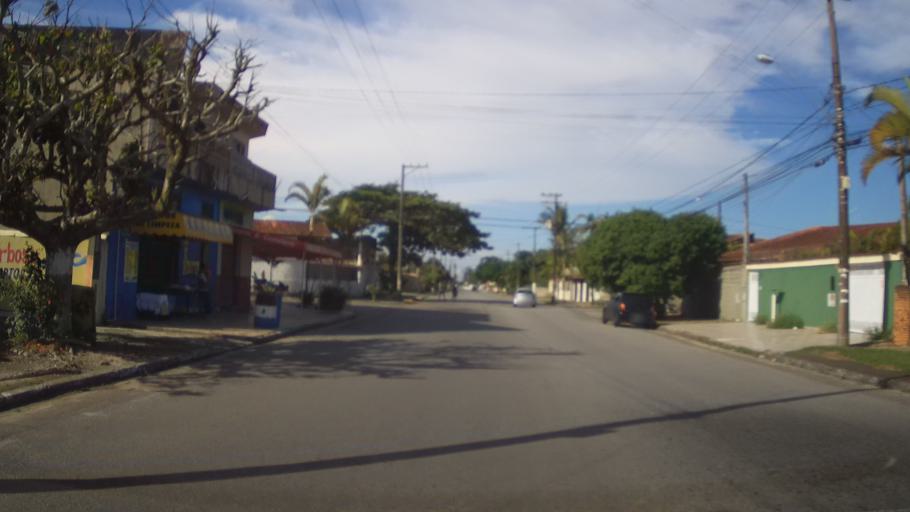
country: BR
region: Sao Paulo
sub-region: Itanhaem
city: Itanhaem
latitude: -24.1720
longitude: -46.7657
